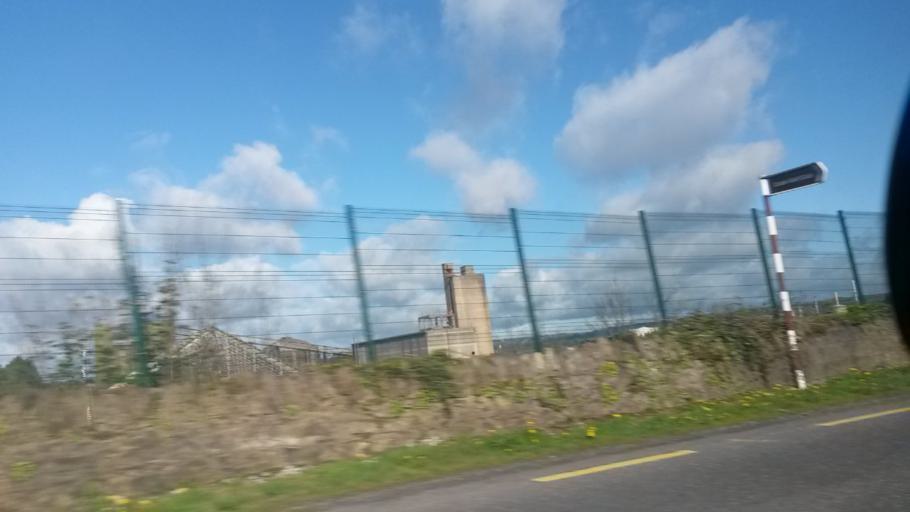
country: IE
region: Munster
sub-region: County Cork
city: Passage West
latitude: 51.8760
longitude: -8.3241
